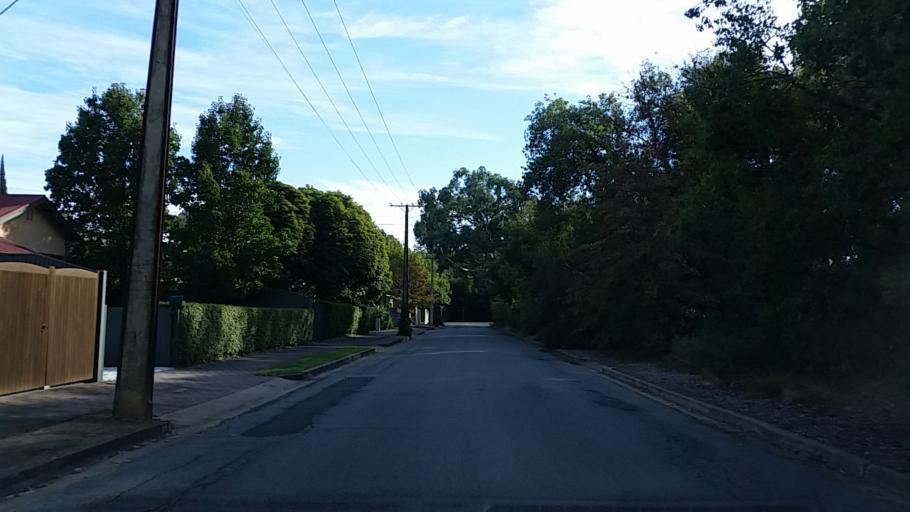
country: AU
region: South Australia
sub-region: Mitcham
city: Hawthorn
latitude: -34.9687
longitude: 138.6025
